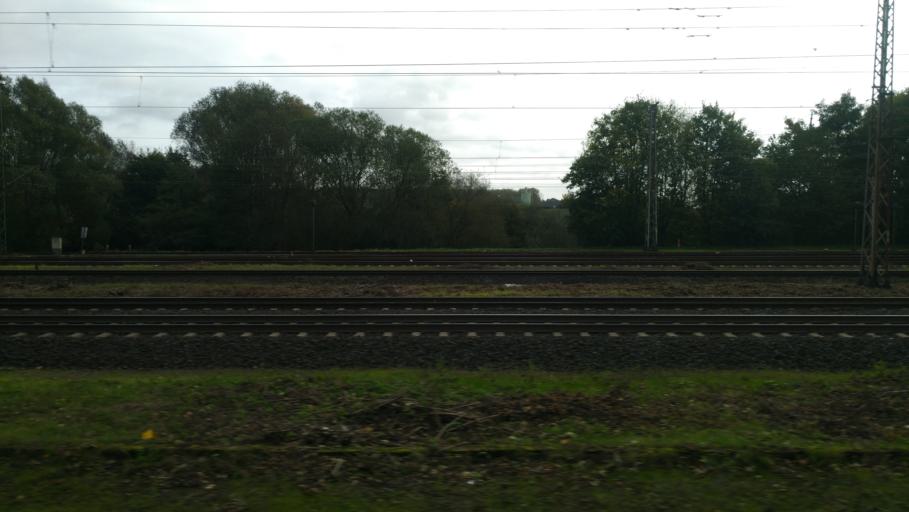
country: DE
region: Lower Saxony
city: Elze
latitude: 52.1238
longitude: 9.7487
